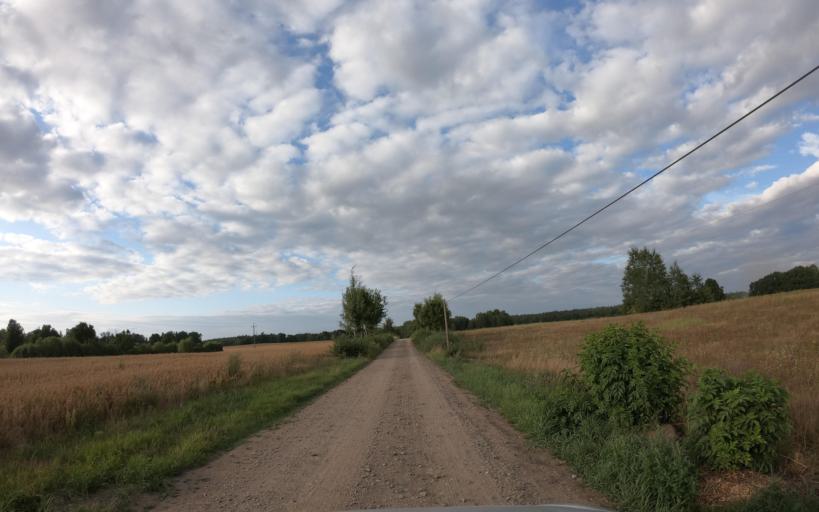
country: PL
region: West Pomeranian Voivodeship
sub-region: Powiat drawski
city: Czaplinek
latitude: 53.5300
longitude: 16.1547
